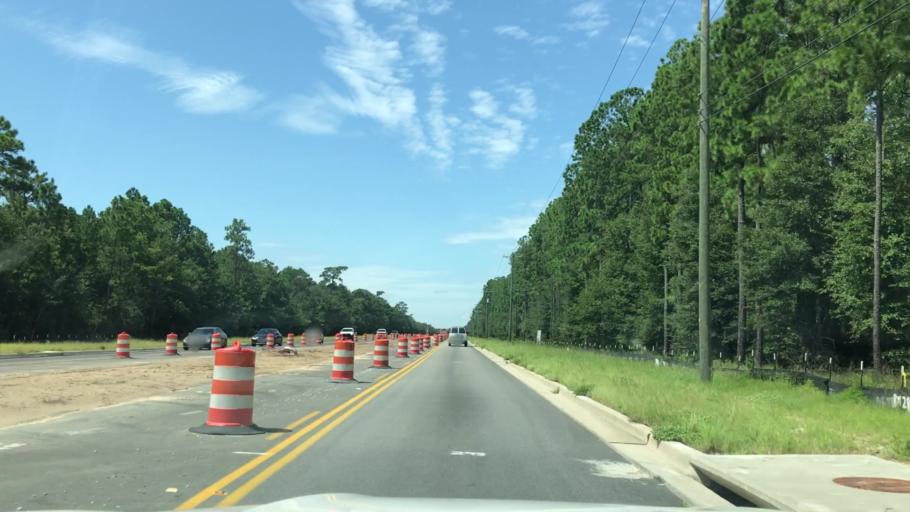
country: US
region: South Carolina
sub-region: Charleston County
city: North Charleston
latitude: 32.9102
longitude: -79.8981
